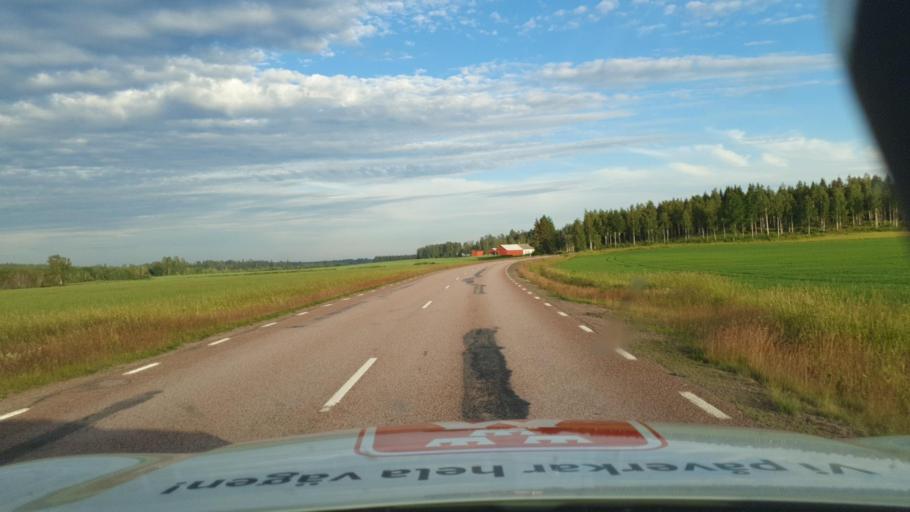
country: SE
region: Vaermland
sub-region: Karlstads Kommun
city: Molkom
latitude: 59.4600
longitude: 13.8235
